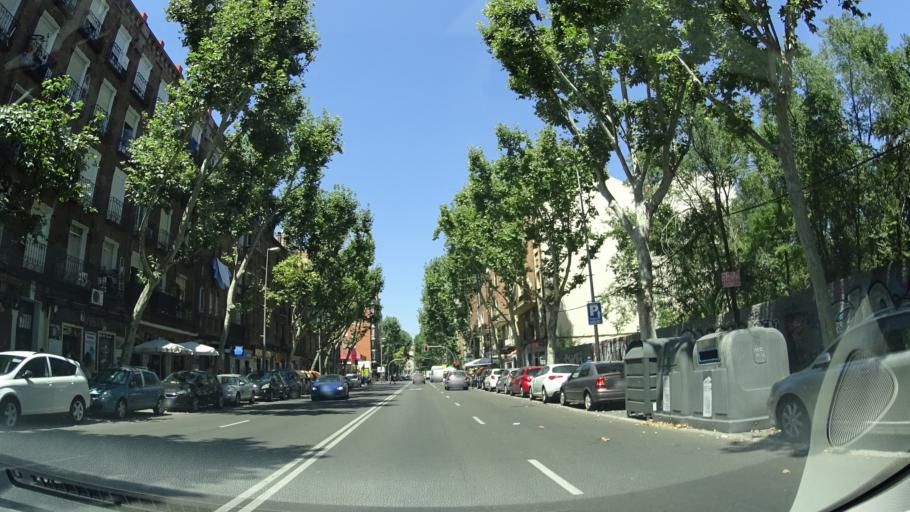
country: ES
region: Madrid
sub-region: Provincia de Madrid
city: Carabanchel
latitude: 40.3963
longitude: -3.7125
